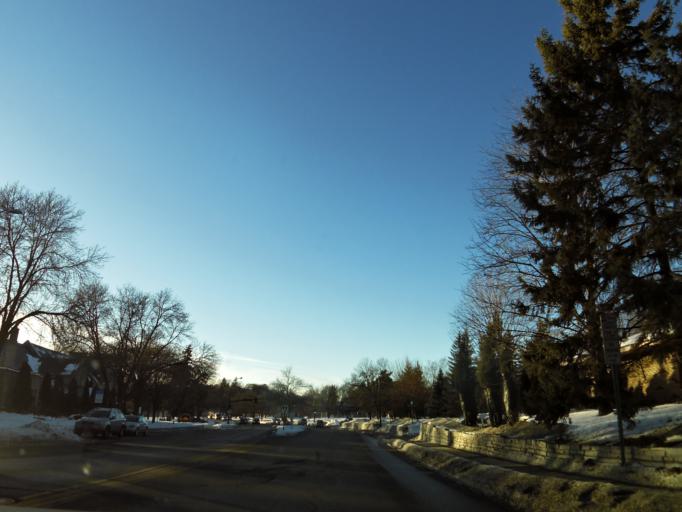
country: US
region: Minnesota
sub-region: Hennepin County
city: Edina
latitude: 44.9125
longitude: -93.3375
